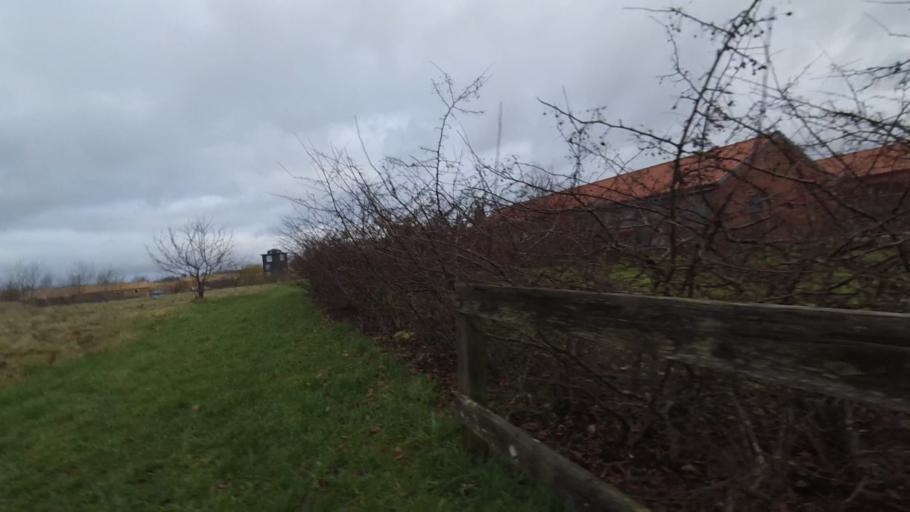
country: DK
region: Central Jutland
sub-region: Arhus Kommune
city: Marslet
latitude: 56.1023
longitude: 10.1706
